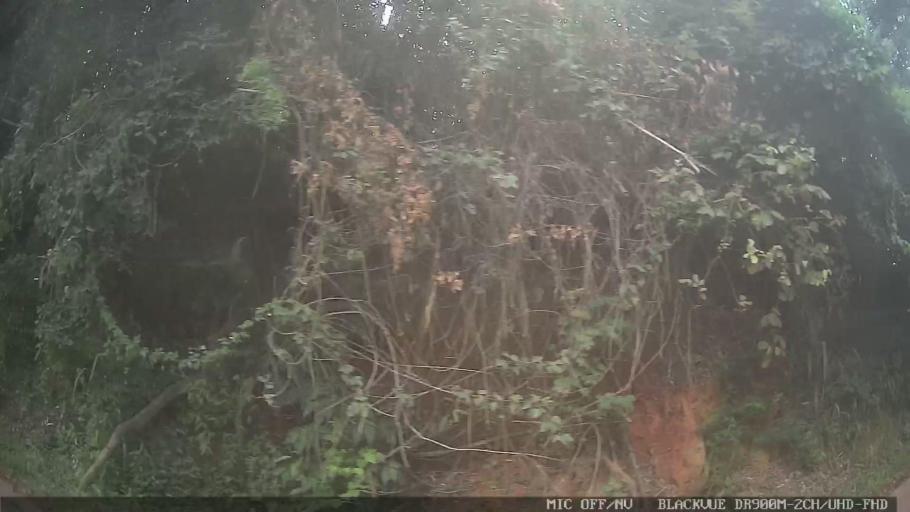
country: BR
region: Sao Paulo
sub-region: Atibaia
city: Atibaia
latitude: -23.0565
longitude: -46.5060
